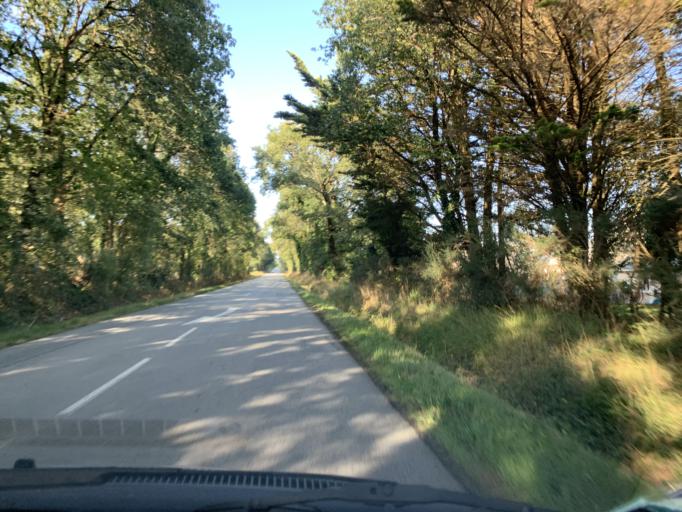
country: FR
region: Brittany
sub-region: Departement du Morbihan
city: Ferel
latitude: 47.4862
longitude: -2.3374
